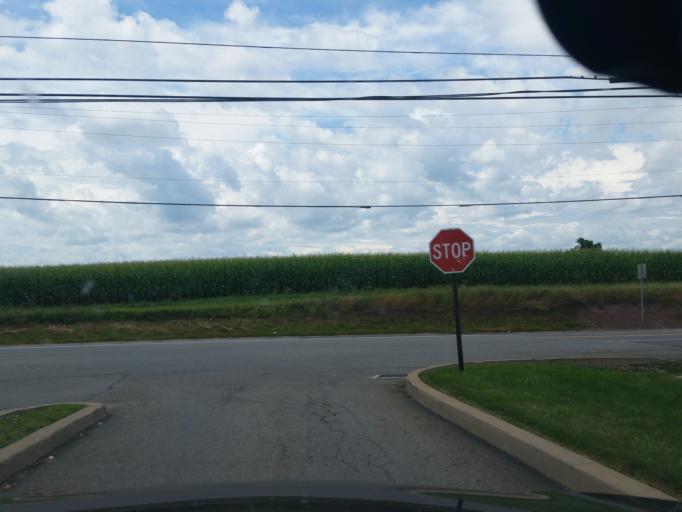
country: US
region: Pennsylvania
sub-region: Dauphin County
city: Elizabethville
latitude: 40.5590
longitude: -76.7894
